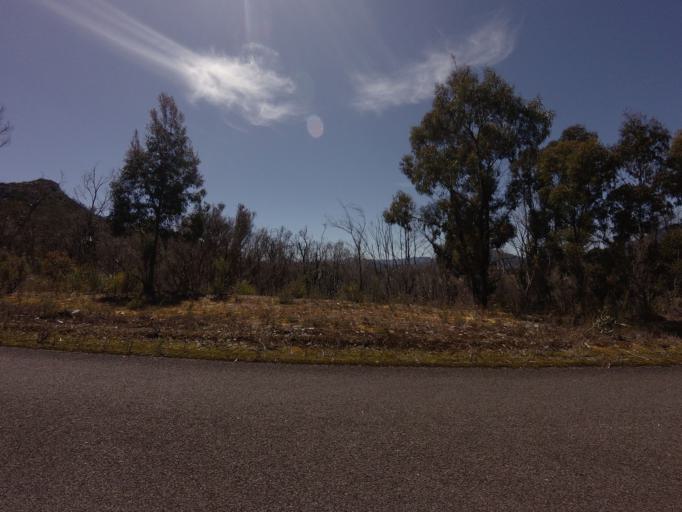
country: AU
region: Tasmania
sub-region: Huon Valley
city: Geeveston
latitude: -42.8531
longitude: 146.1866
